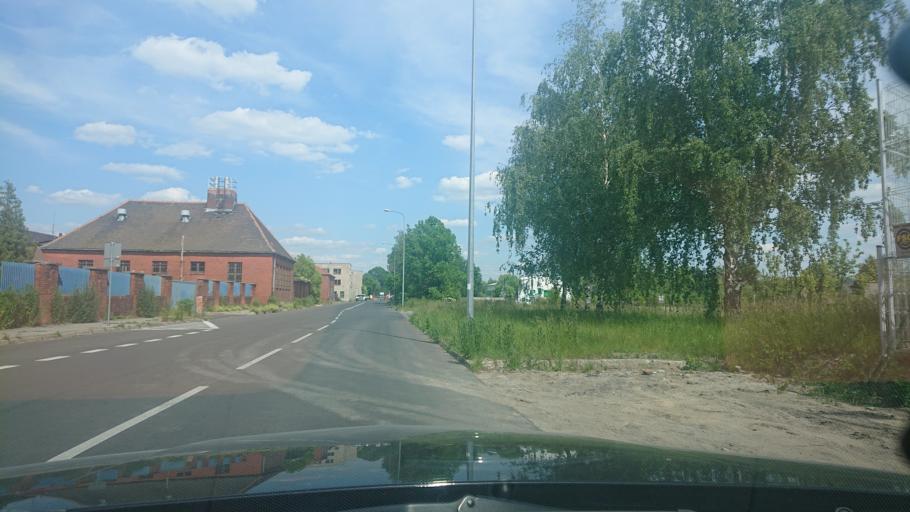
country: PL
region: Greater Poland Voivodeship
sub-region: Powiat gnieznienski
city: Gniezno
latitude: 52.5276
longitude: 17.6001
